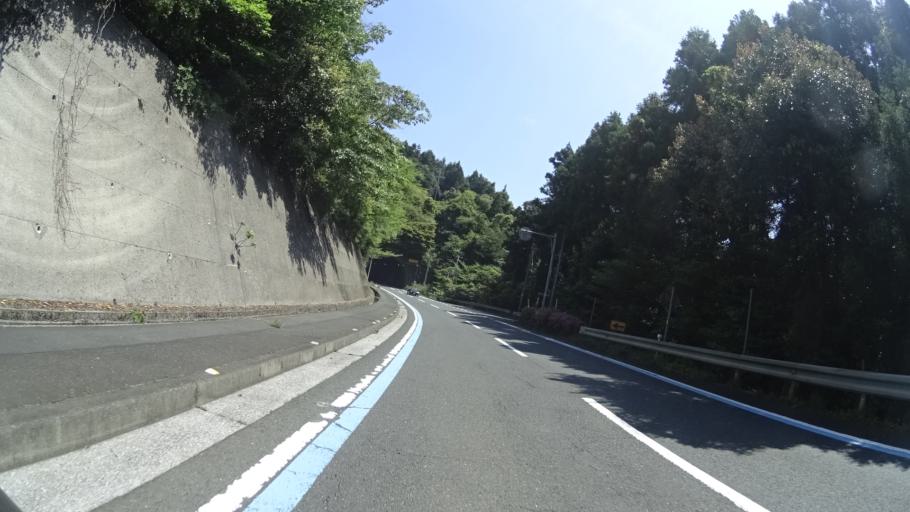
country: JP
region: Ehime
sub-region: Nishiuwa-gun
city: Ikata-cho
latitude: 33.4362
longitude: 132.2339
